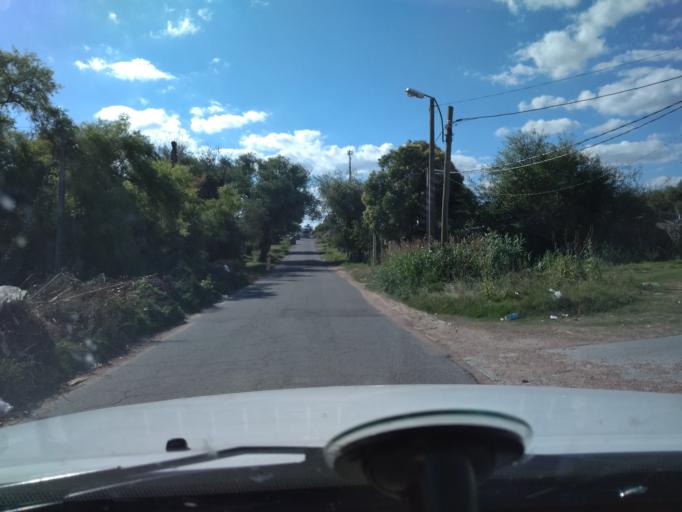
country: UY
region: Canelones
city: La Paz
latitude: -34.8128
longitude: -56.2029
